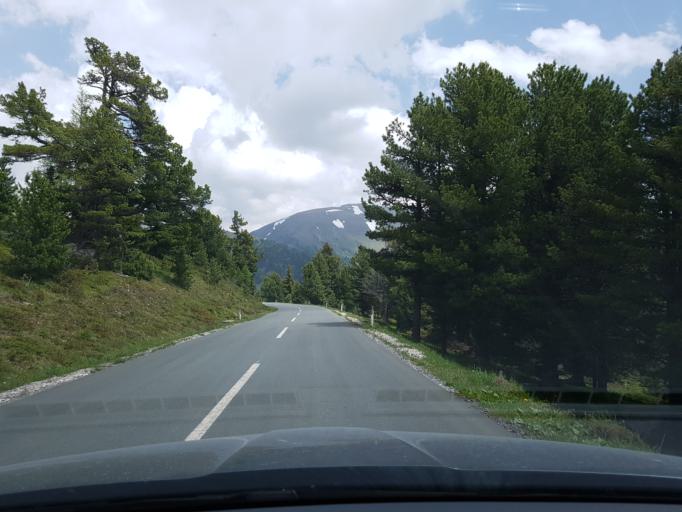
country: AT
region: Carinthia
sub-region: Politischer Bezirk Spittal an der Drau
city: Kleinkirchheim
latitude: 46.8887
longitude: 13.8109
